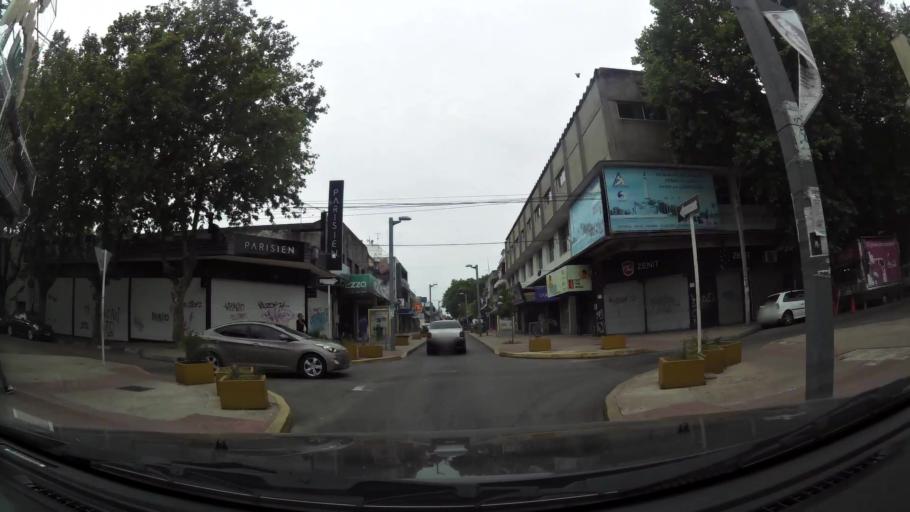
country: UY
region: Canelones
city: Las Piedras
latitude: -34.7270
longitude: -56.2182
